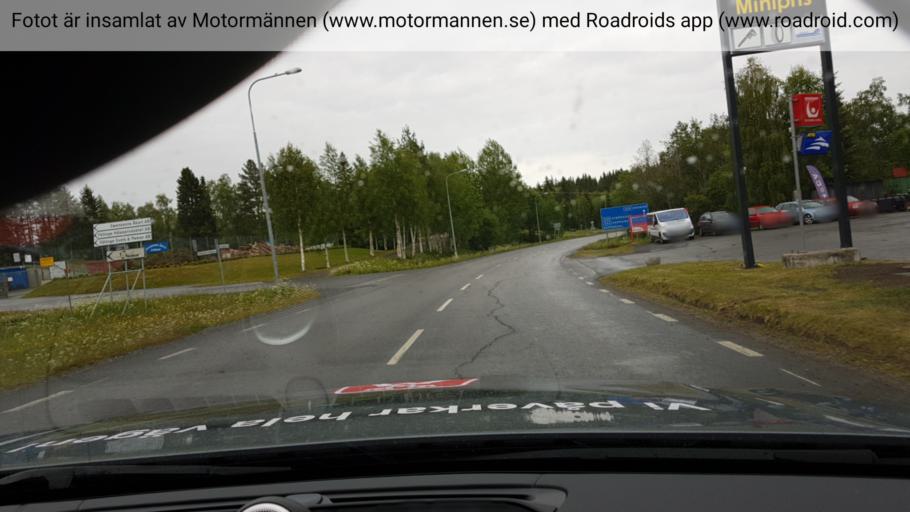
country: SE
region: Jaemtland
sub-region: Krokoms Kommun
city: Krokom
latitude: 63.6713
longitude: 14.6208
